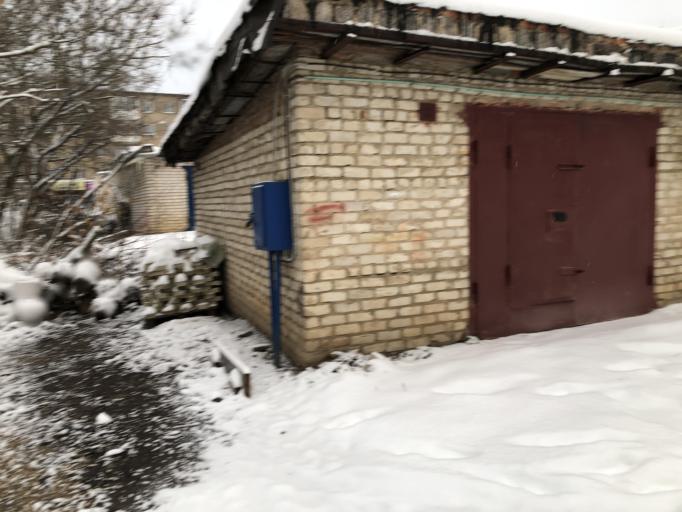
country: RU
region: Smolensk
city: Safonovo
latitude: 55.1143
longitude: 33.2288
